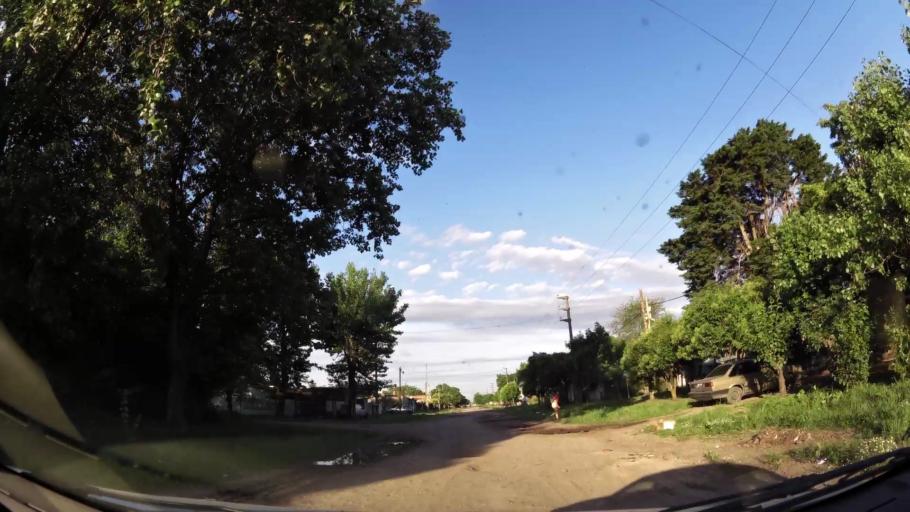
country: AR
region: Buenos Aires
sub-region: Partido de Merlo
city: Merlo
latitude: -34.6937
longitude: -58.7497
